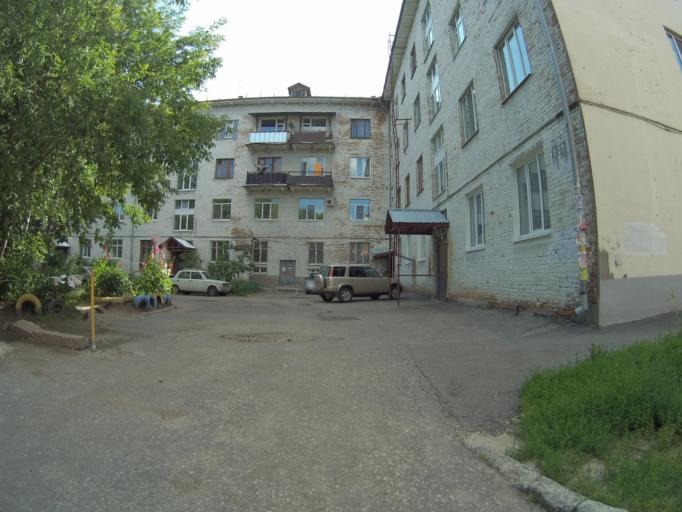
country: RU
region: Vladimir
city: Vladimir
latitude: 56.1413
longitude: 40.3954
